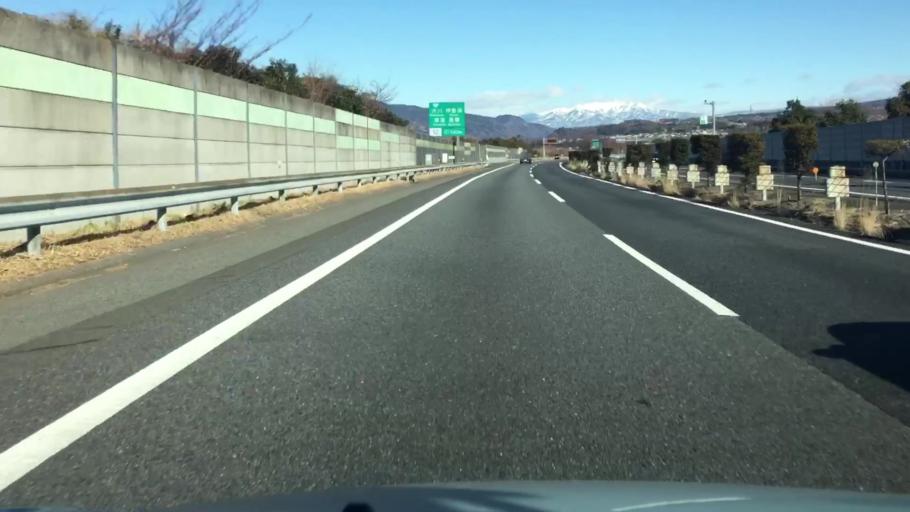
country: JP
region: Gunma
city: Shibukawa
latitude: 36.4684
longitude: 139.0119
